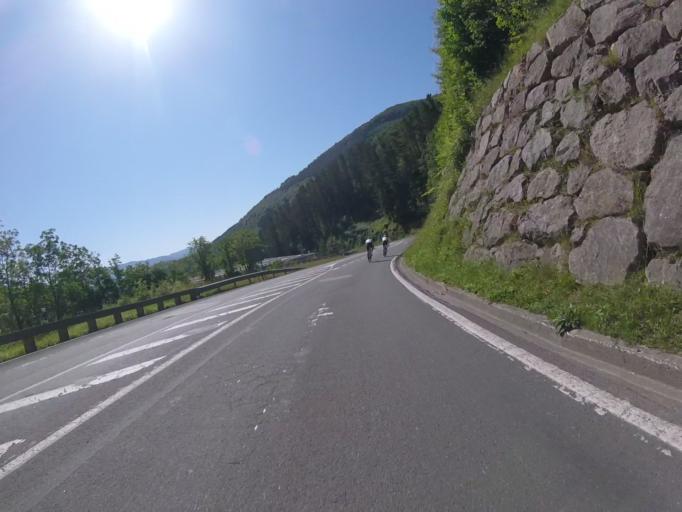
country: ES
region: Basque Country
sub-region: Provincia de Guipuzcoa
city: Albiztur
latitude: 43.1256
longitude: -2.1212
